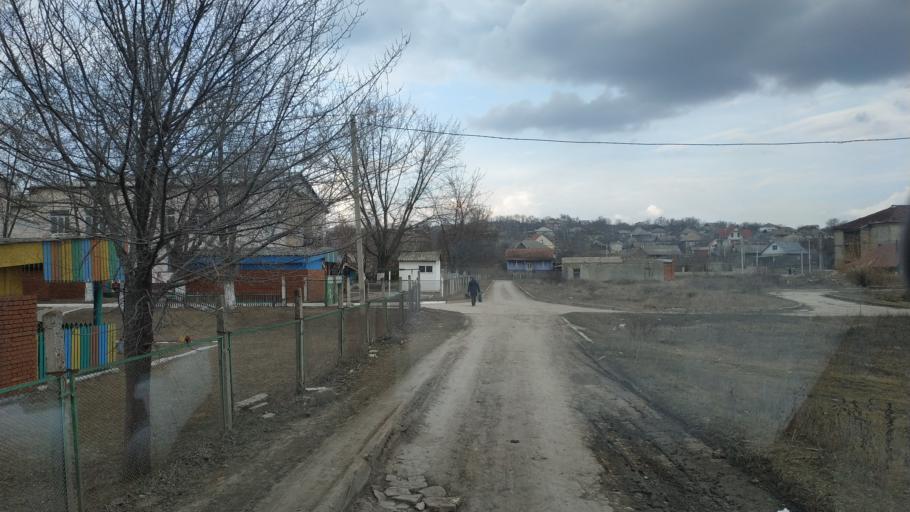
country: MD
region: Anenii Noi
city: Varnita
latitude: 46.8396
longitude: 29.3607
